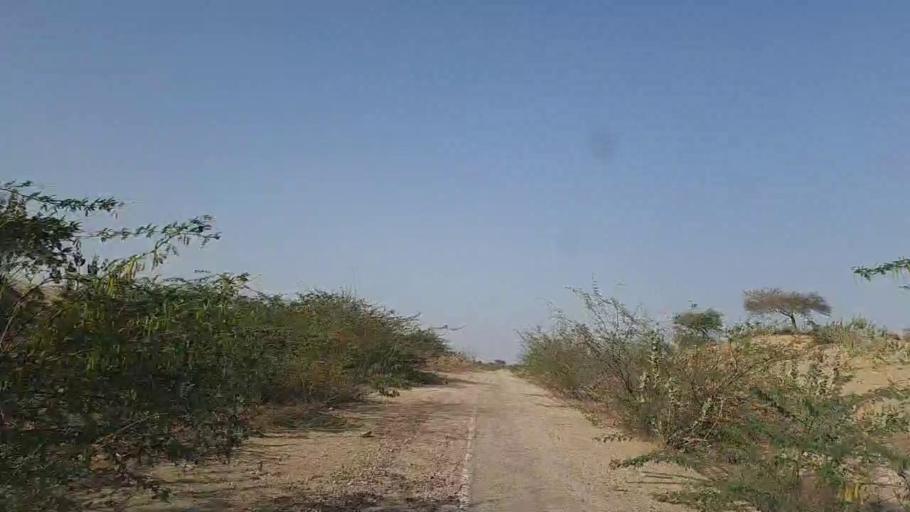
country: PK
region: Sindh
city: Naukot
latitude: 24.6166
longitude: 69.3474
